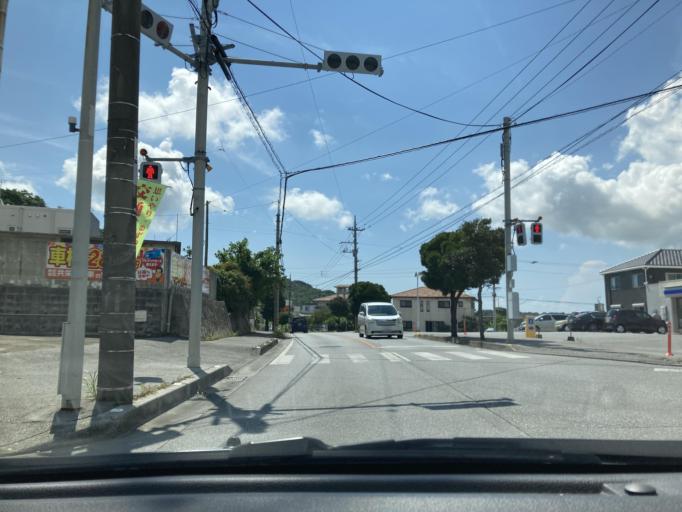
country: JP
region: Okinawa
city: Tomigusuku
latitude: 26.1661
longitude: 127.7547
